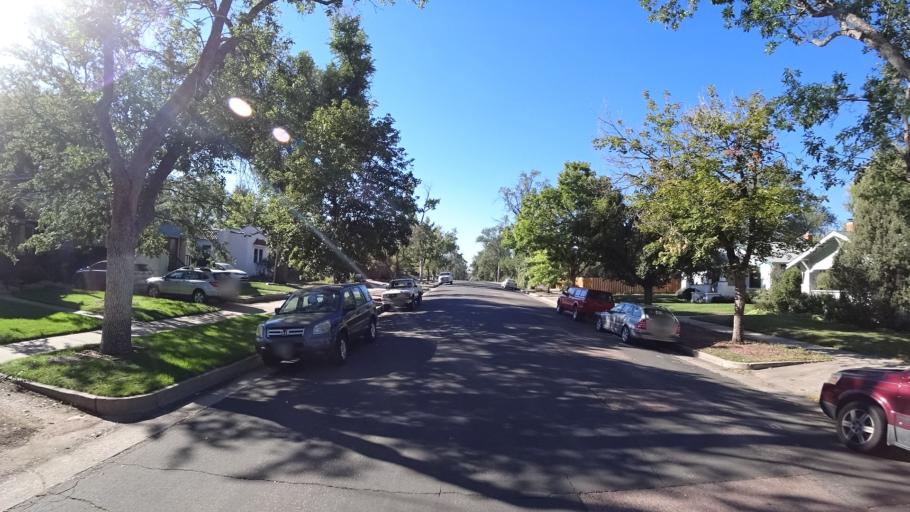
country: US
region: Colorado
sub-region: El Paso County
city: Colorado Springs
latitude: 38.8426
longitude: -104.8063
